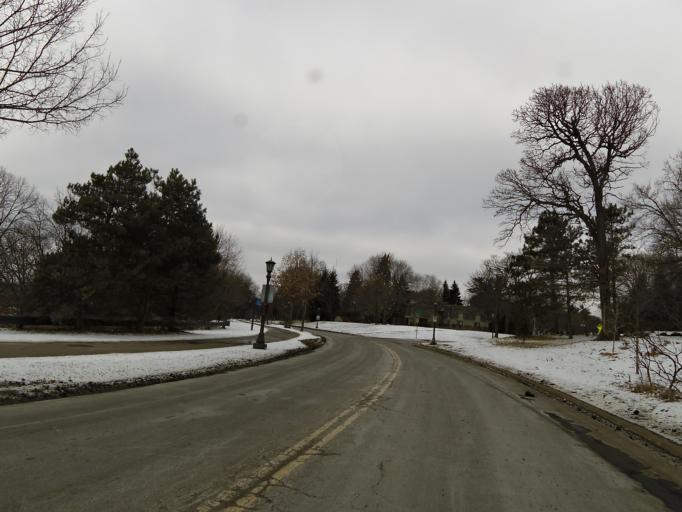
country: US
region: Minnesota
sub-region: Ramsey County
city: Lauderdale
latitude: 44.9501
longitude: -93.2000
